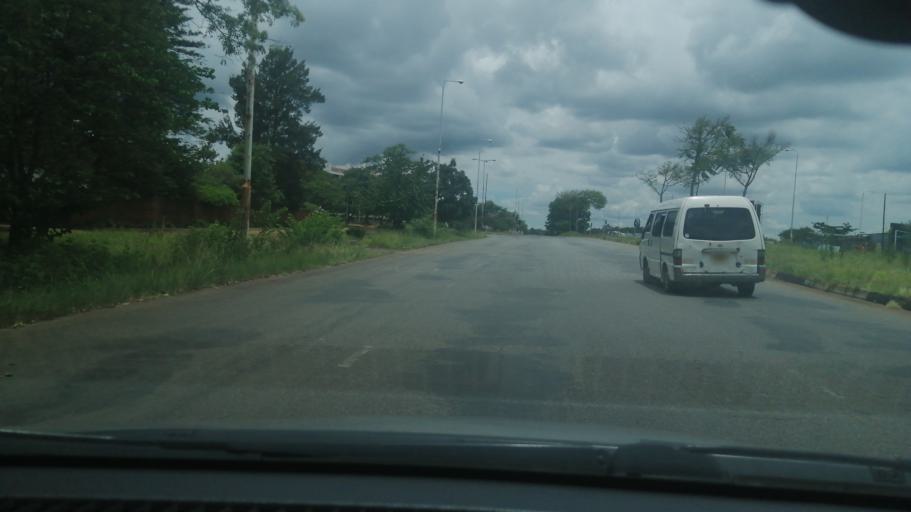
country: ZW
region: Harare
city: Harare
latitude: -17.8331
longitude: 31.0862
